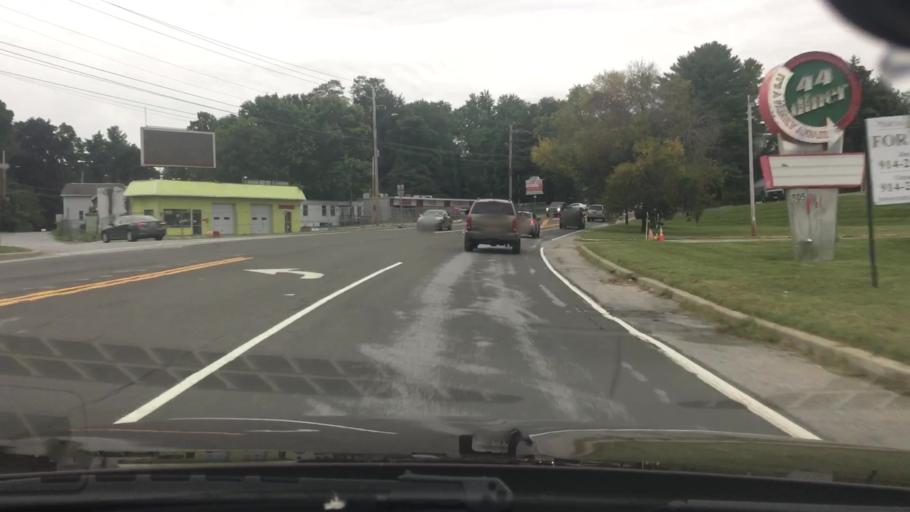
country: US
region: New York
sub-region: Dutchess County
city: Arlington
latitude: 41.7020
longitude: -73.8719
